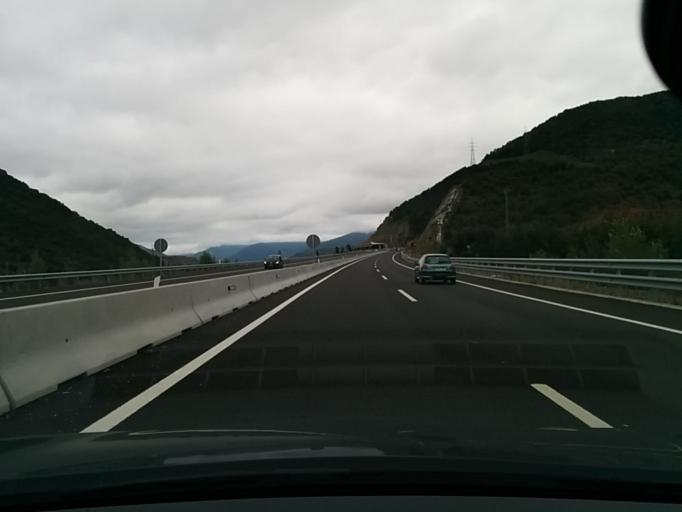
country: ES
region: Aragon
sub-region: Provincia de Huesca
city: Sabinanigo
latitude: 42.4883
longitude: -0.3716
